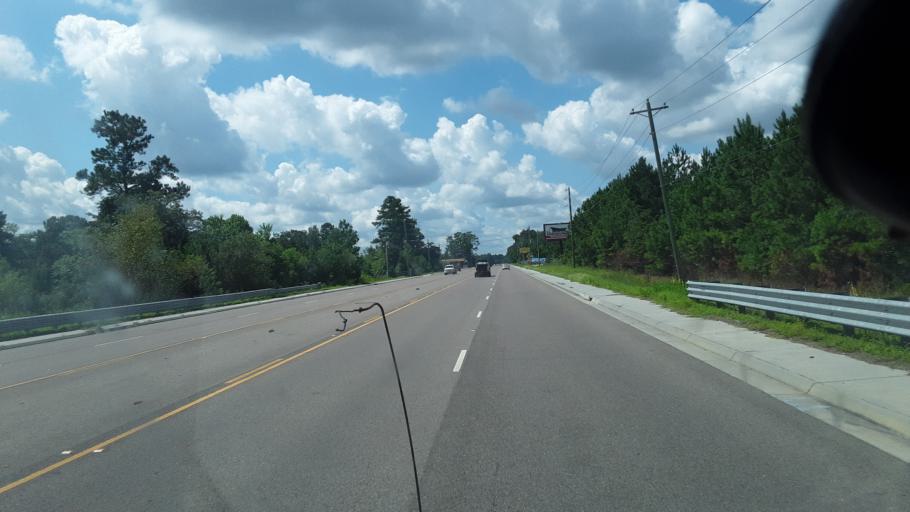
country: US
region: South Carolina
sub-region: Berkeley County
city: Moncks Corner
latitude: 33.1699
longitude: -80.0427
